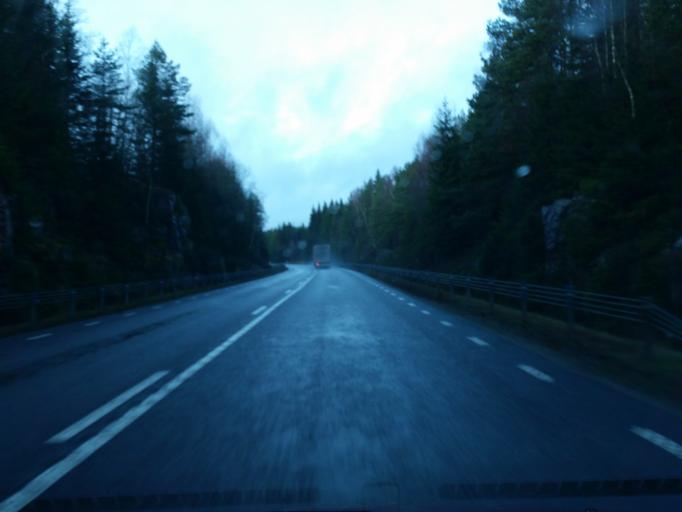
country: SE
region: Joenkoeping
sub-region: Gislaveds Kommun
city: Gislaved
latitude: 57.3348
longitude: 13.5177
